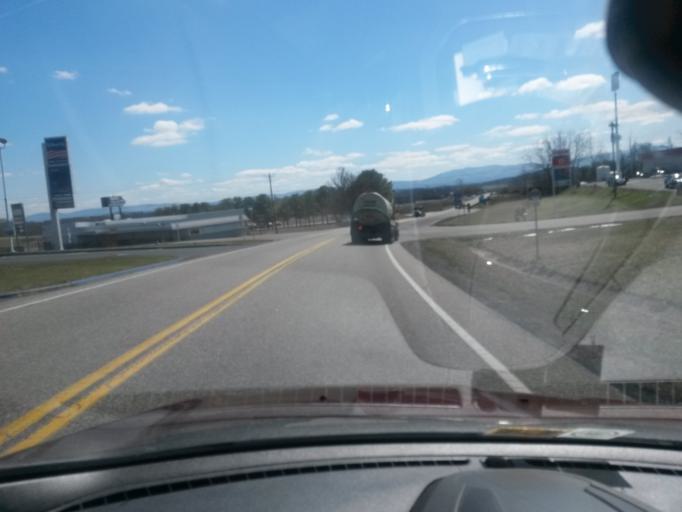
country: US
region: Virginia
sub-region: Augusta County
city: Jolivue
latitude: 38.0782
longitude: -79.0897
